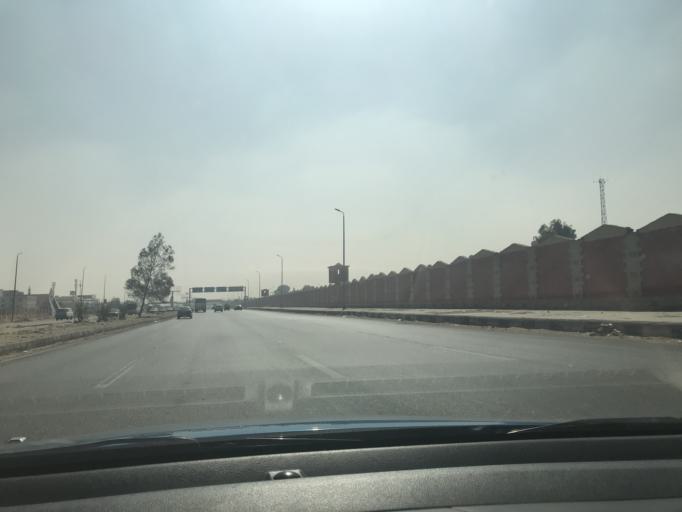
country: EG
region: Muhafazat al Qalyubiyah
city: Al Khankah
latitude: 30.1582
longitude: 31.4585
